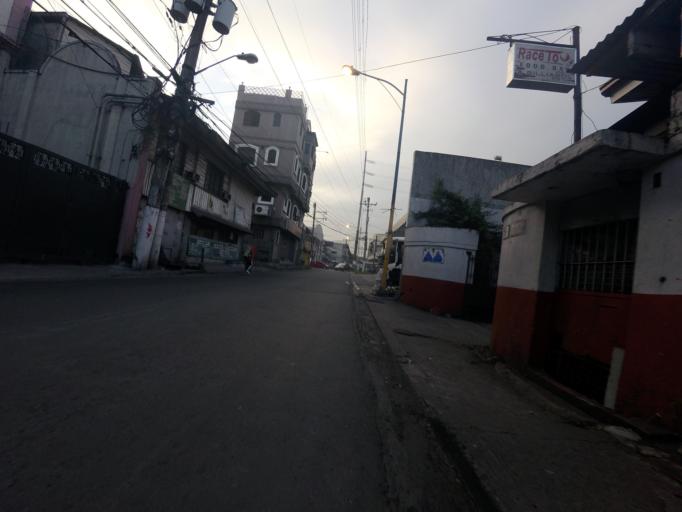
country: PH
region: Metro Manila
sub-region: San Juan
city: San Juan
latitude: 14.5948
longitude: 121.0283
